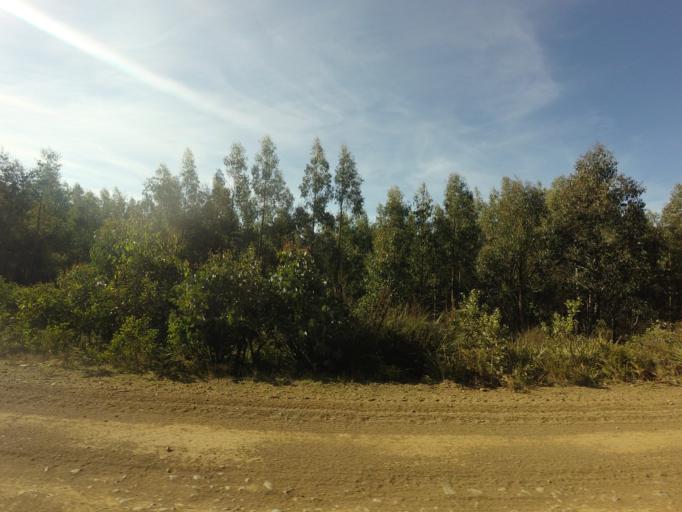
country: AU
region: Tasmania
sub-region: Sorell
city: Sorell
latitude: -42.5004
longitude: 147.5366
